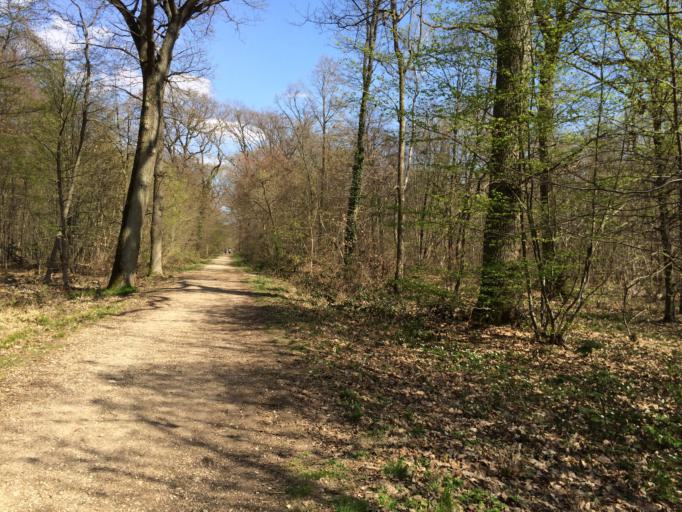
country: FR
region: Ile-de-France
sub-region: Departement de l'Essonne
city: Draveil
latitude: 48.6706
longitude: 2.4261
